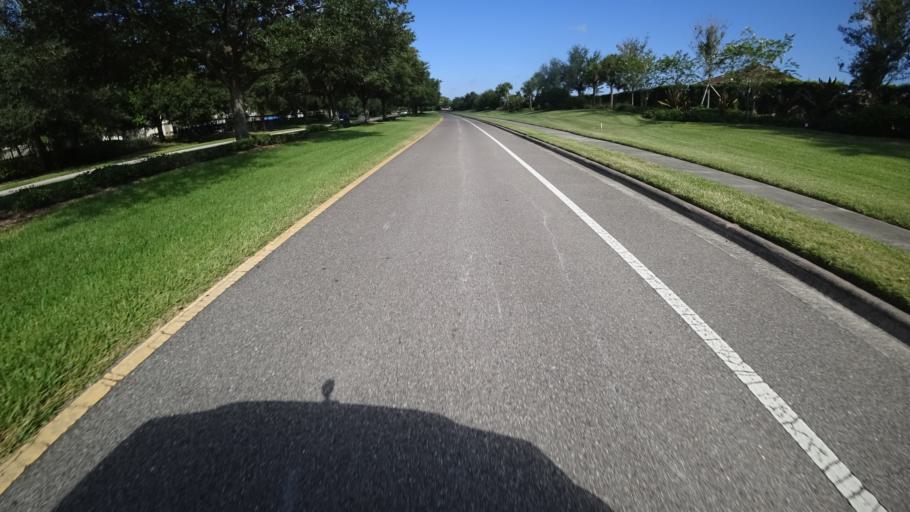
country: US
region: Florida
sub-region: Manatee County
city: Ellenton
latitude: 27.5054
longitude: -82.4748
